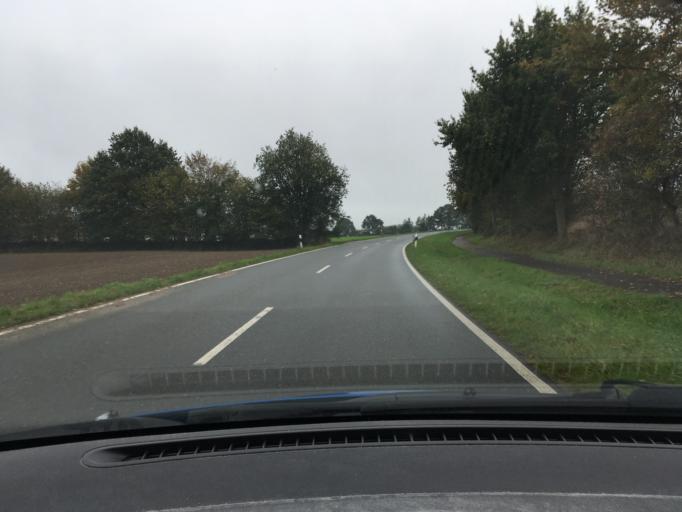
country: DE
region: Schleswig-Holstein
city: Bosdorf
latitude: 54.1101
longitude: 10.4795
